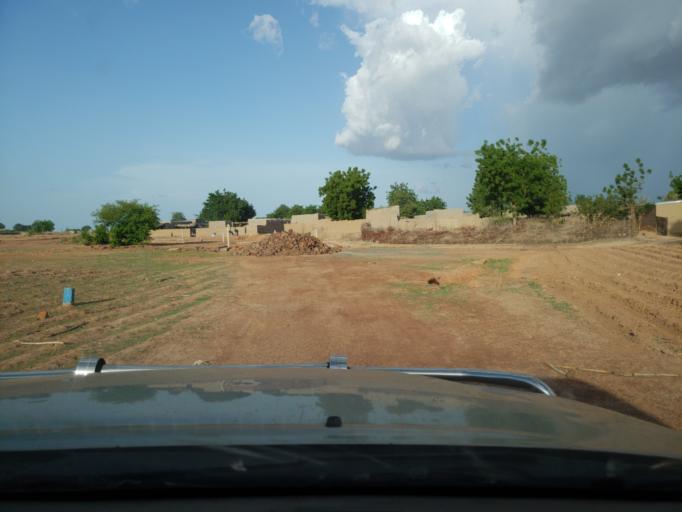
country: ML
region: Segou
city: Bla
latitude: 12.7357
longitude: -5.6563
